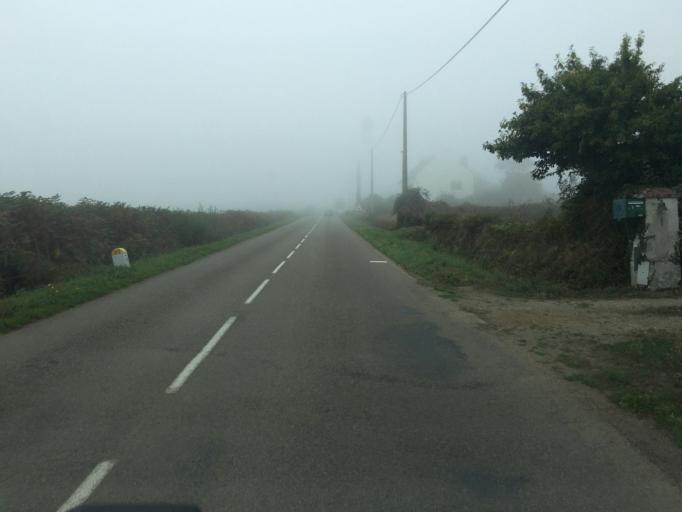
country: FR
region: Brittany
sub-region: Departement du Finistere
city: Plogoff
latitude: 48.0629
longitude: -4.6383
